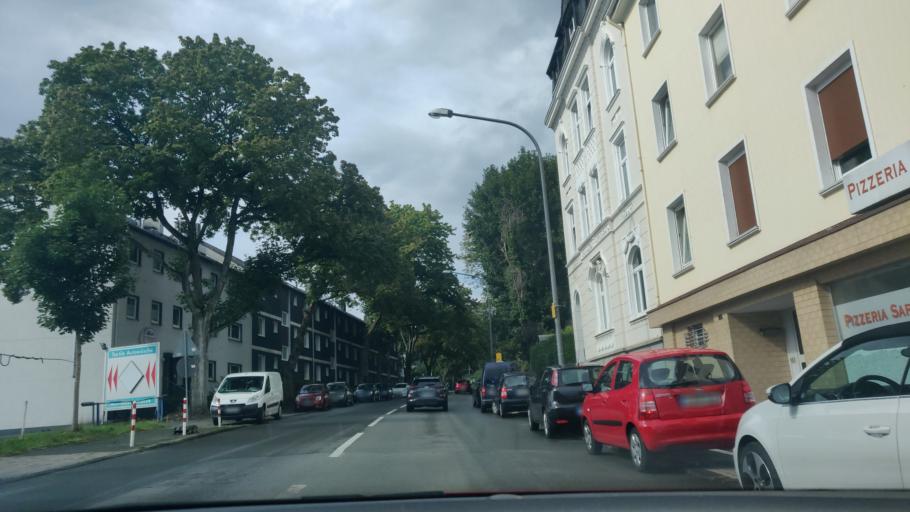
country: DE
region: North Rhine-Westphalia
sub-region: Regierungsbezirk Dusseldorf
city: Wuppertal
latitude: 51.2717
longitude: 7.1247
